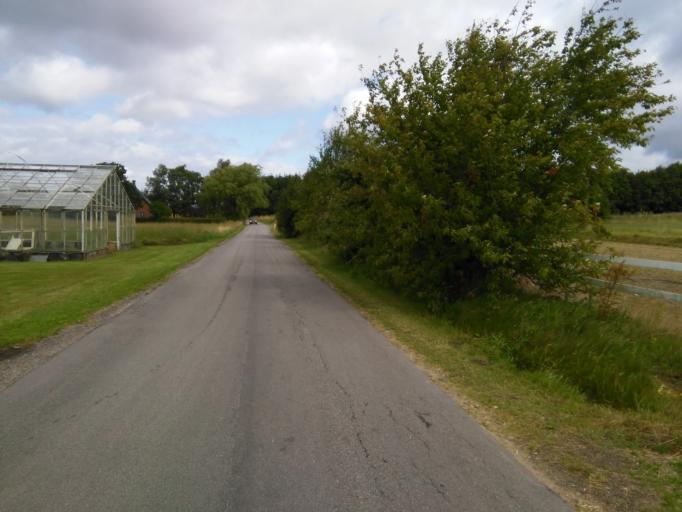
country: DK
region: Central Jutland
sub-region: Arhus Kommune
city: Marslet
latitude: 56.0893
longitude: 10.1585
